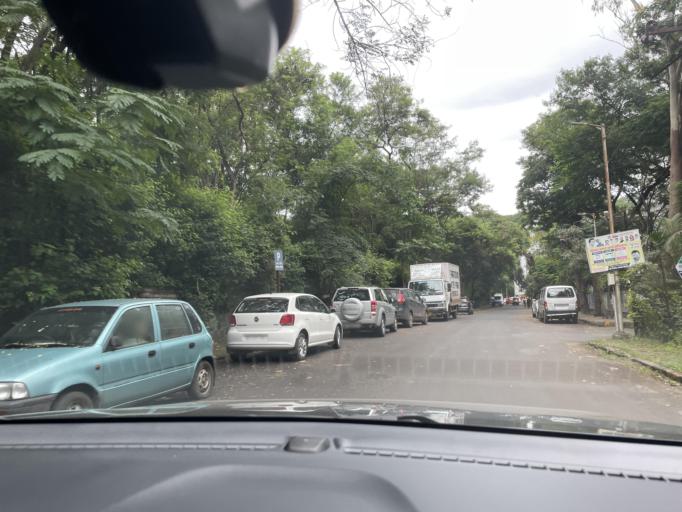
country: IN
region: Maharashtra
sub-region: Pune Division
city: Shivaji Nagar
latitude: 18.5320
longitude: 73.8141
